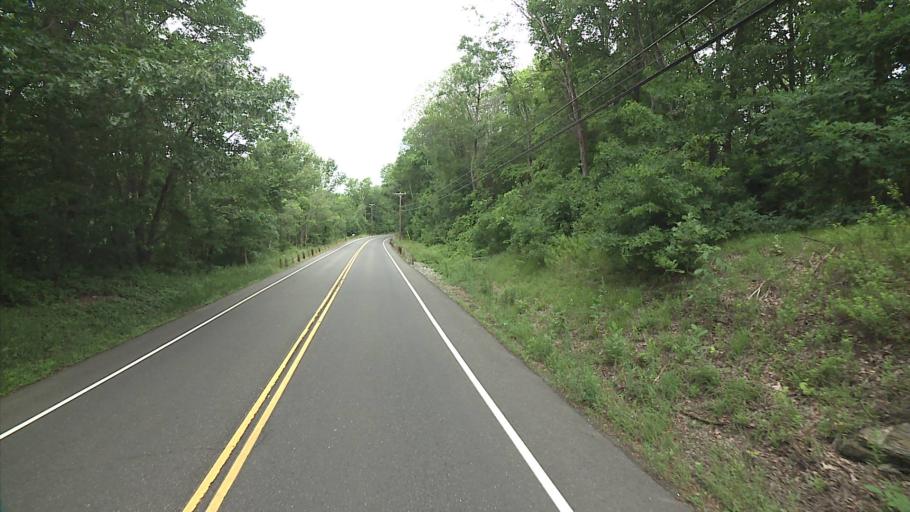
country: US
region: Connecticut
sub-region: Litchfield County
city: Bethlehem Village
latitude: 41.6641
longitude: -73.1600
